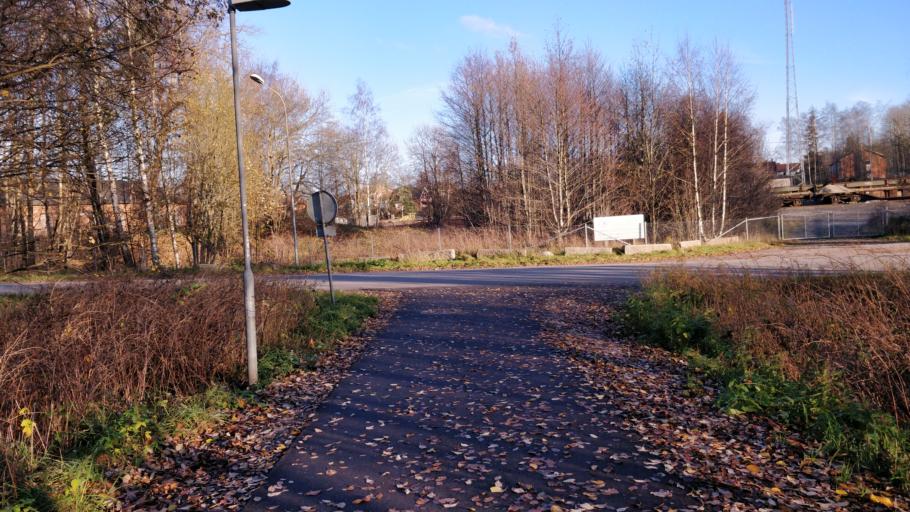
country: SE
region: Kronoberg
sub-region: Almhults Kommun
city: AElmhult
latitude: 56.5461
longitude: 14.1333
